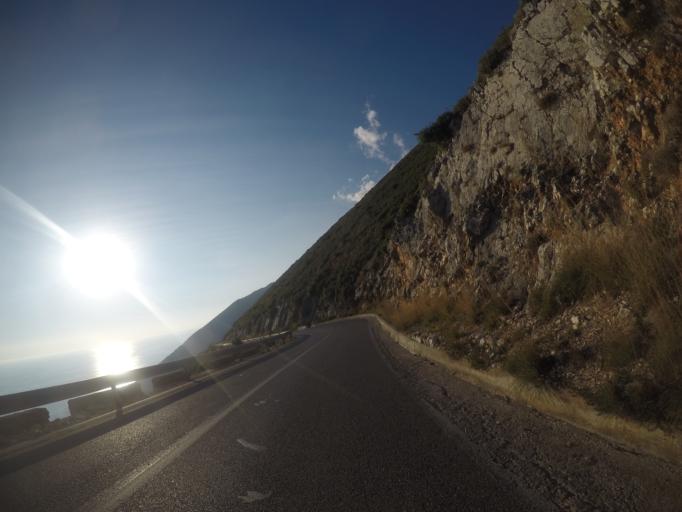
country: AL
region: Vlore
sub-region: Rrethi i Vlores
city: Vranisht
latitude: 40.1796
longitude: 19.5984
